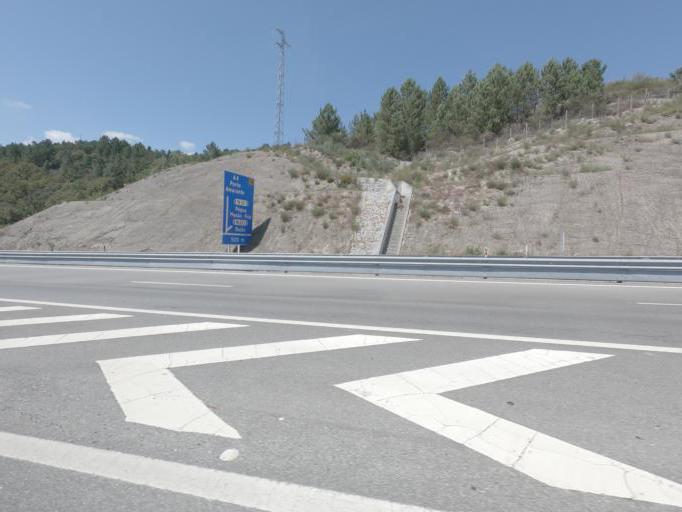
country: PT
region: Porto
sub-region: Amarante
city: Amarante
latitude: 41.2552
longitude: -8.0412
